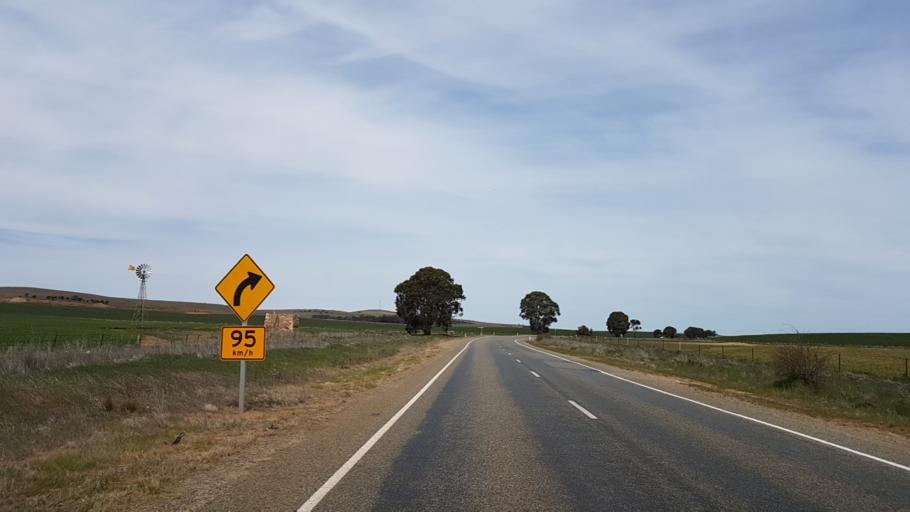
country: AU
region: South Australia
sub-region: Northern Areas
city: Jamestown
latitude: -33.0877
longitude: 138.6194
